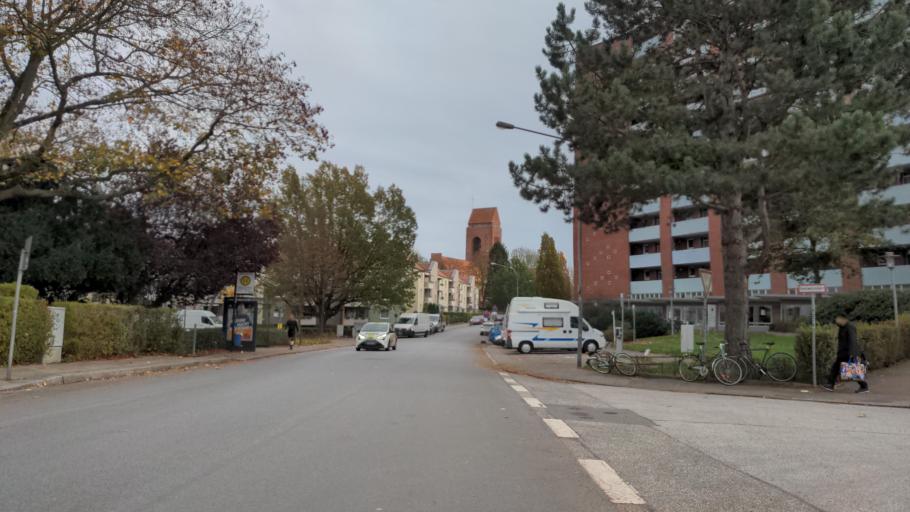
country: DE
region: Schleswig-Holstein
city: Luebeck
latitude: 53.8556
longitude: 10.6607
